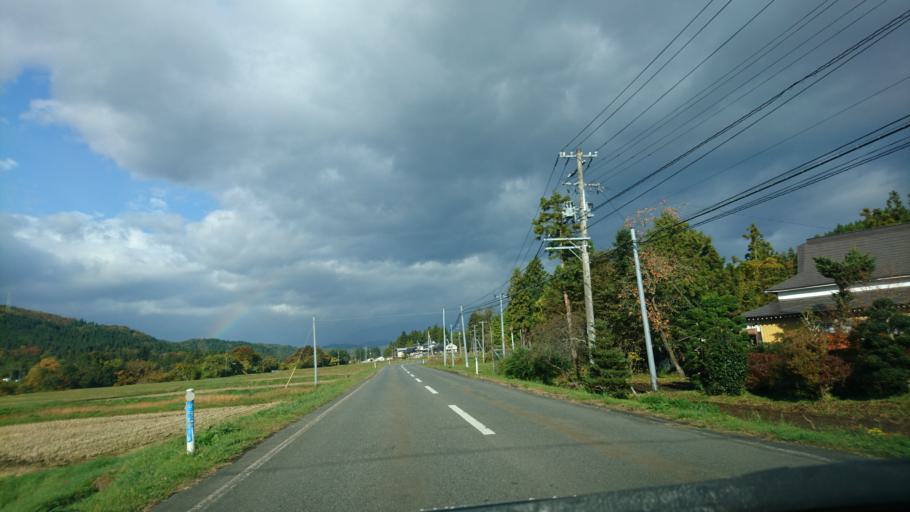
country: JP
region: Iwate
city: Mizusawa
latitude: 39.0718
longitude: 141.0196
